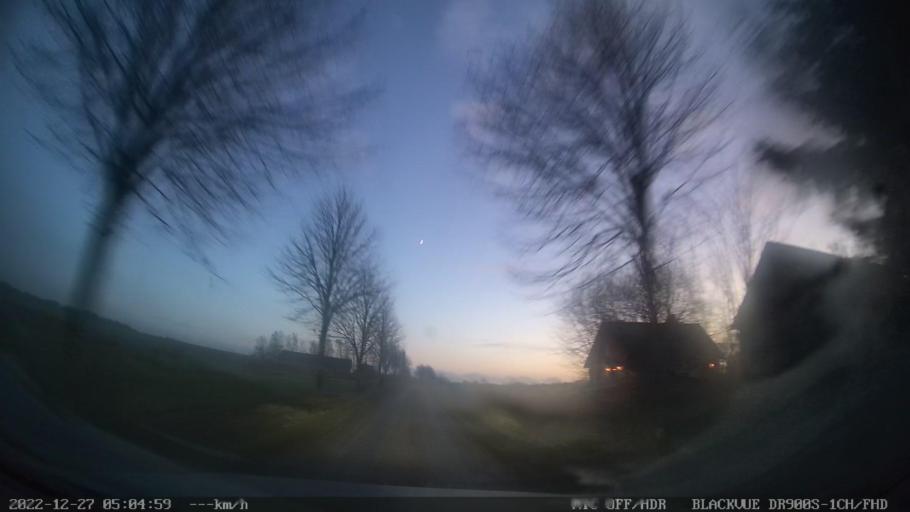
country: SE
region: Skane
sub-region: Simrishamns Kommun
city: Kivik
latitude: 55.5815
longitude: 14.1266
